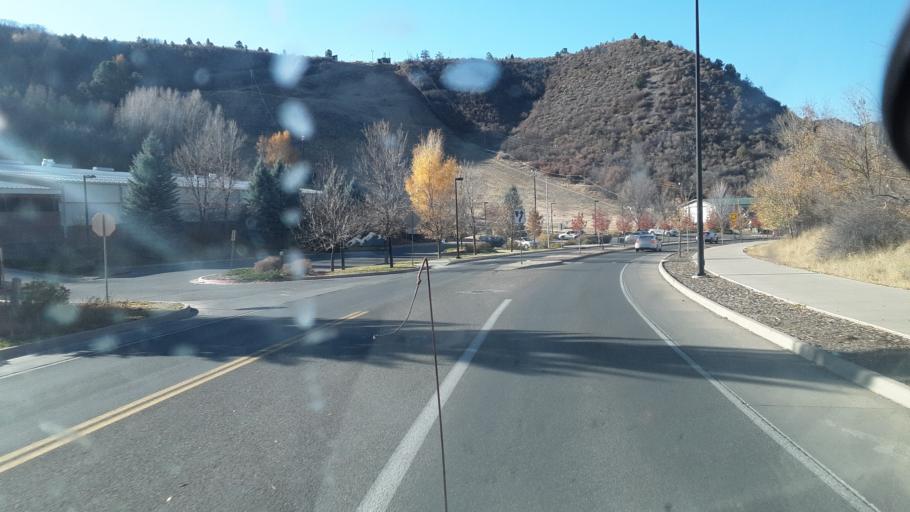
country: US
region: Colorado
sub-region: La Plata County
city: Durango
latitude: 37.2844
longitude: -107.8676
